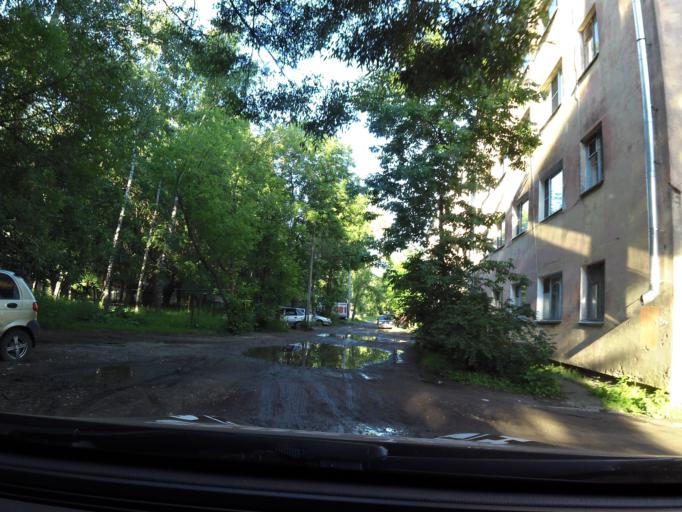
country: RU
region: Vologda
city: Vologda
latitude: 59.2192
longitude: 39.9148
